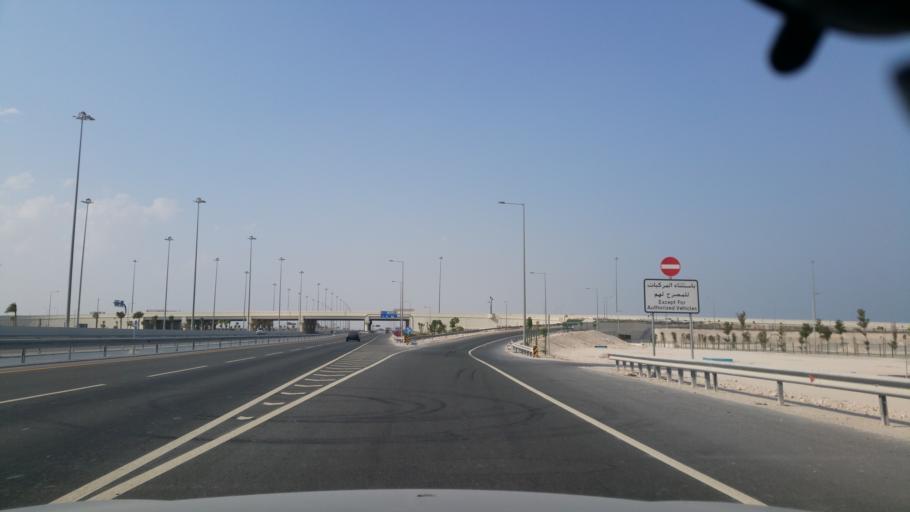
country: QA
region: Baladiyat Umm Salal
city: Umm Salal `Ali
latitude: 25.4536
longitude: 51.4798
